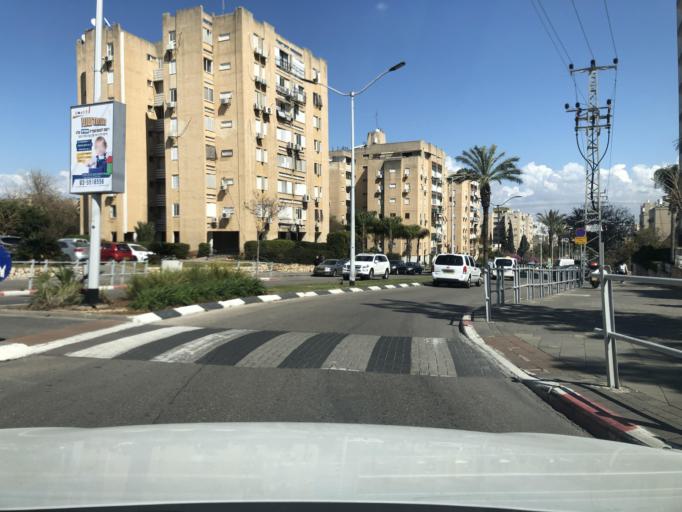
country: IL
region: Tel Aviv
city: Bat Yam
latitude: 32.0094
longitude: 34.7552
